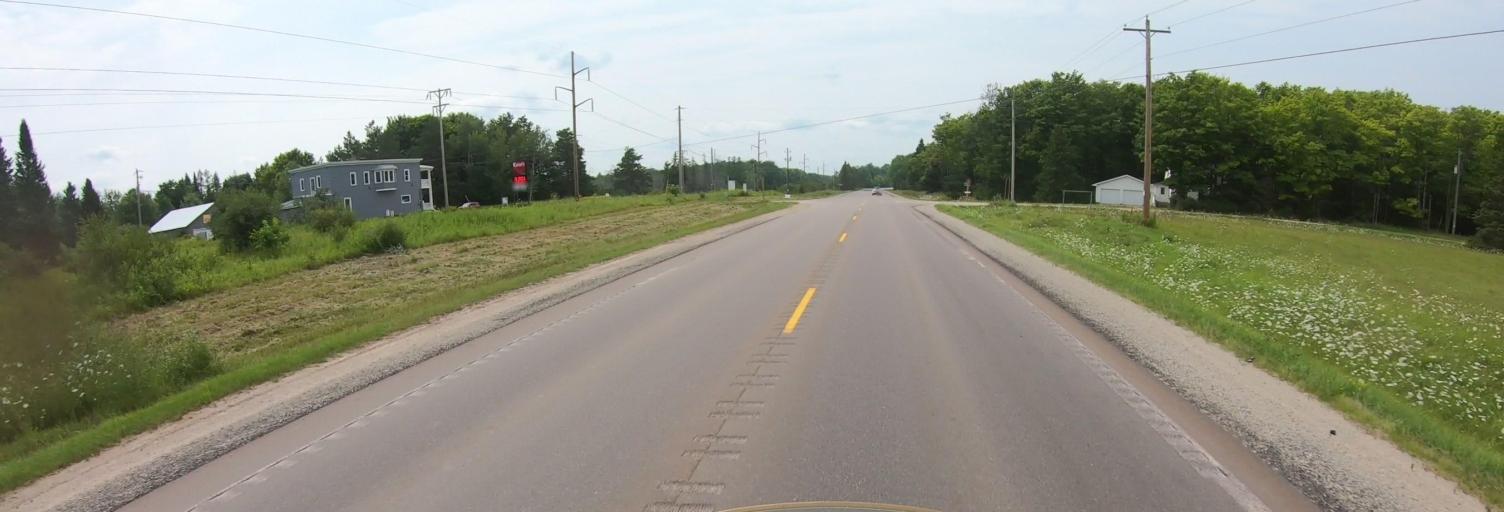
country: US
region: Michigan
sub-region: Marquette County
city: Harvey
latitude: 46.3491
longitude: -87.0323
